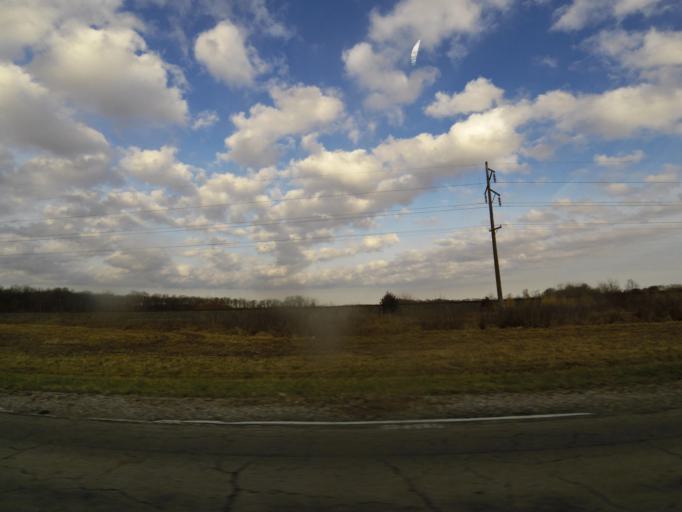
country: US
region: Illinois
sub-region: Bond County
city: Greenville
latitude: 38.9131
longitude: -89.2994
